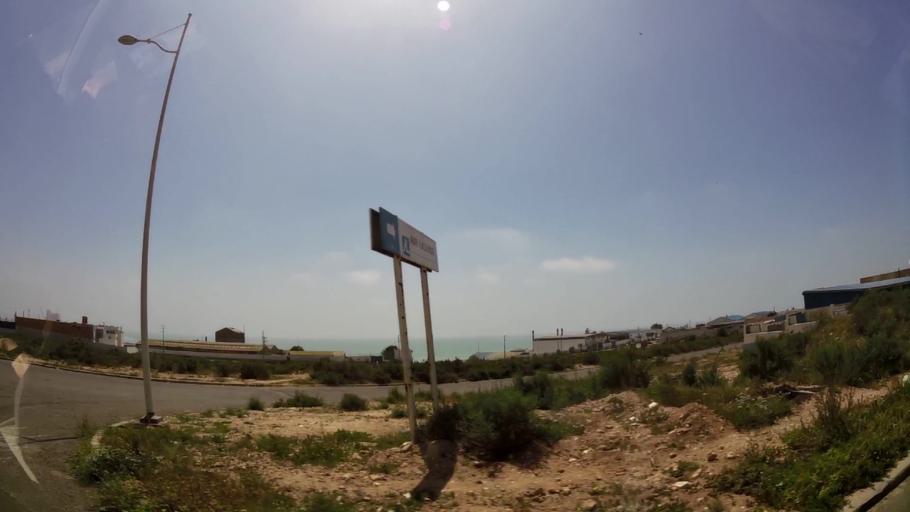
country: MA
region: Souss-Massa-Draa
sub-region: Agadir-Ida-ou-Tnan
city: Aourir
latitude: 30.4417
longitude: -9.6475
